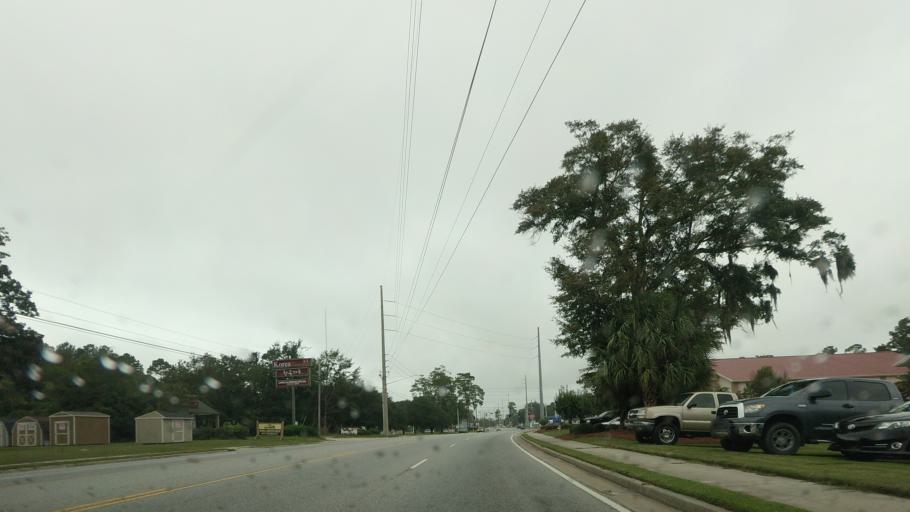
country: US
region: Georgia
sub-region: Lowndes County
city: Remerton
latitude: 30.8276
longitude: -83.3082
